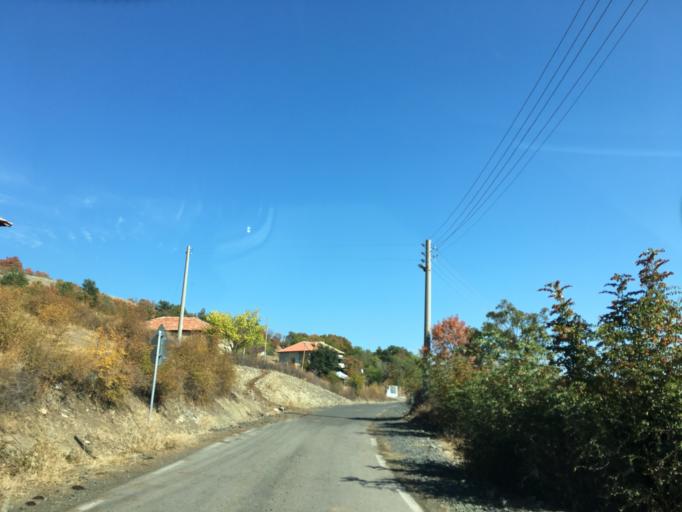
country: BG
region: Kurdzhali
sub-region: Obshtina Krumovgrad
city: Krumovgrad
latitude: 41.5066
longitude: 25.5238
